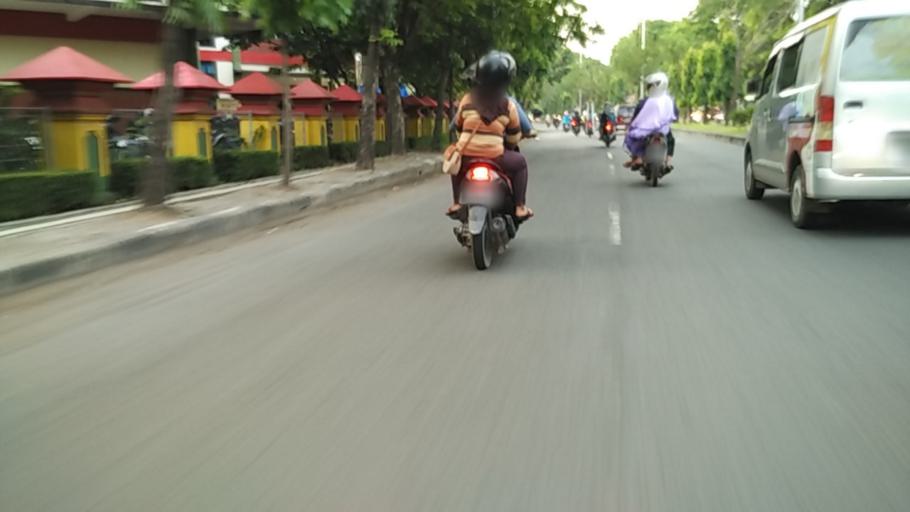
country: ID
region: Central Java
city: Semarang
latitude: -6.9809
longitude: 110.4525
